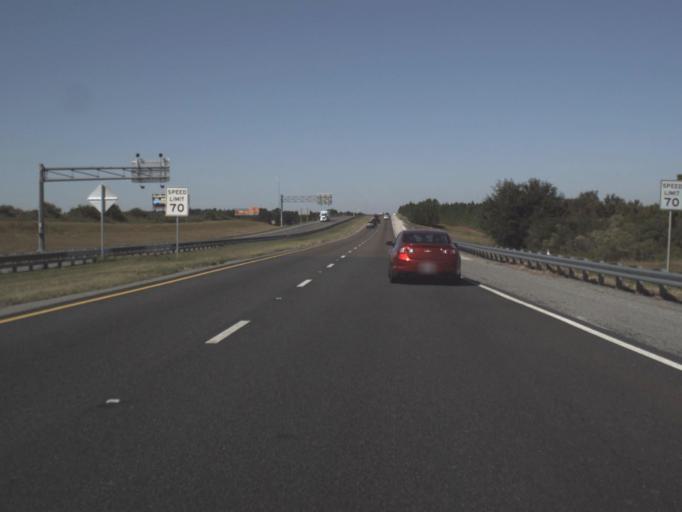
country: US
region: Florida
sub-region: Lake County
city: Yalaha
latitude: 28.6722
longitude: -81.8469
